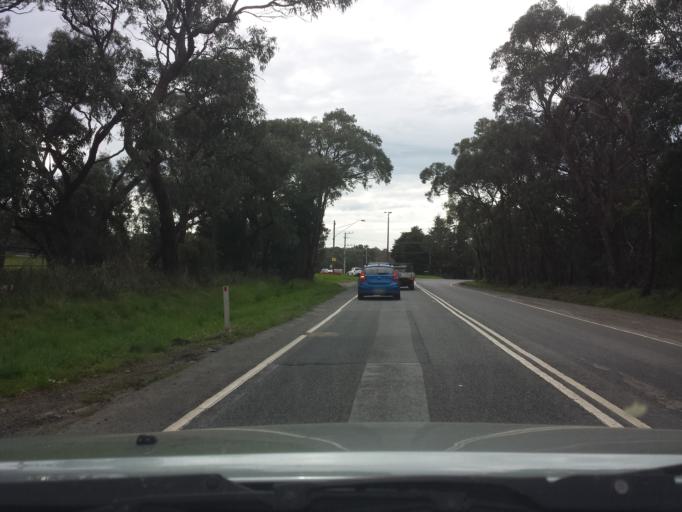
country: AU
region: Victoria
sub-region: Yarra Ranges
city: Belgrave South
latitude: -37.9552
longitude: 145.3471
